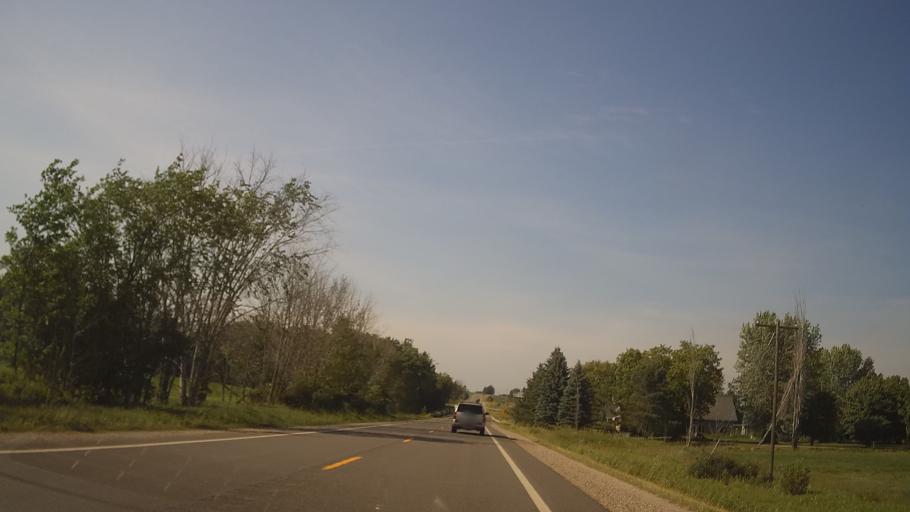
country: US
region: Michigan
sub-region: Ogemaw County
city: West Branch
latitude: 44.3459
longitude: -84.1258
